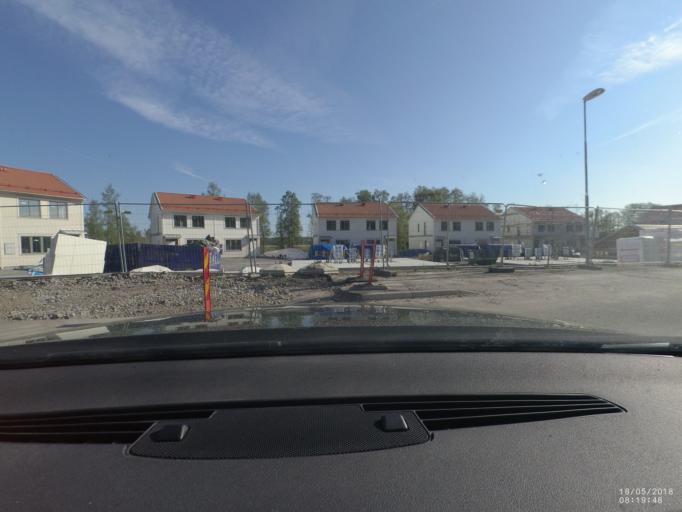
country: SE
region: Soedermanland
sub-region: Nykopings Kommun
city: Nykoping
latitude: 58.7374
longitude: 17.0162
